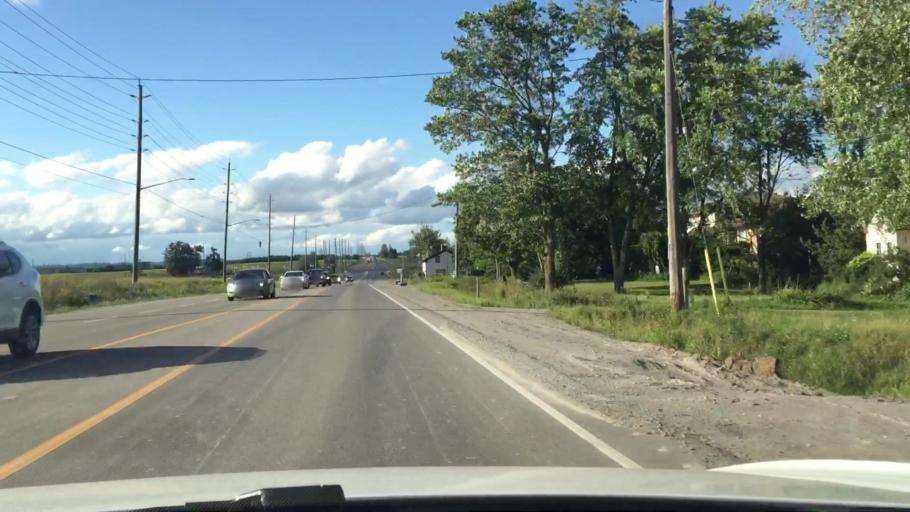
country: CA
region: Ontario
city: Oshawa
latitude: 43.9520
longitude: -78.8550
